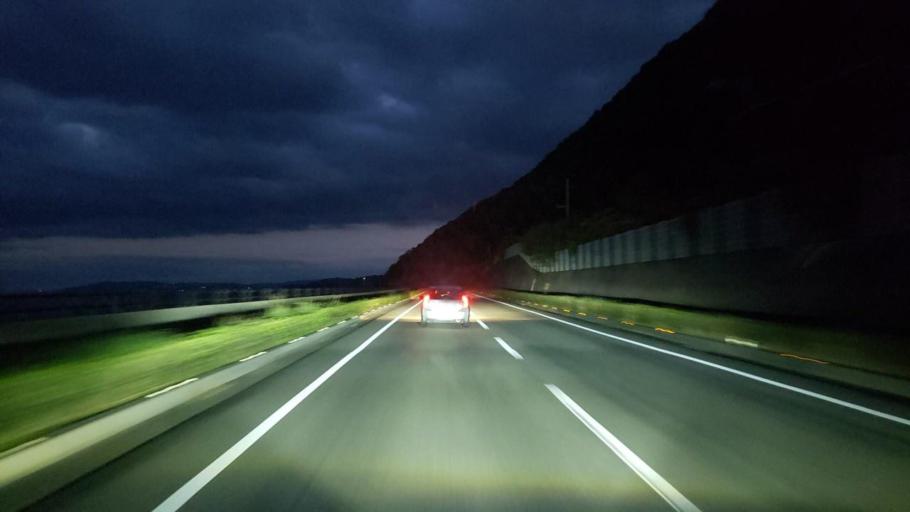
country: JP
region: Tokushima
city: Narutocho-mitsuishi
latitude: 34.2247
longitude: 134.4985
